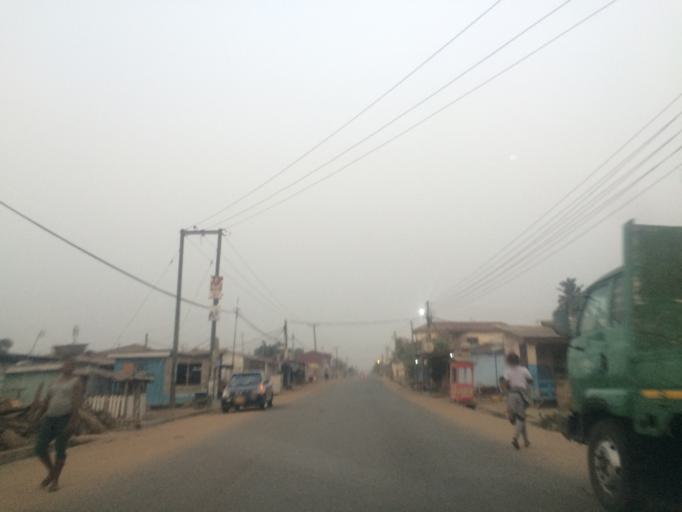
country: GH
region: Greater Accra
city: Teshi Old Town
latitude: 5.5914
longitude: -0.1028
